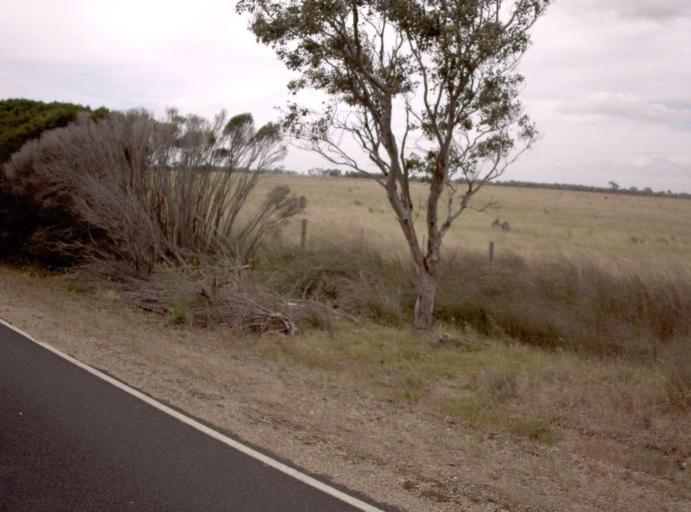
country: AU
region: Victoria
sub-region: Wellington
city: Sale
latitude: -37.9653
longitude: 147.1319
